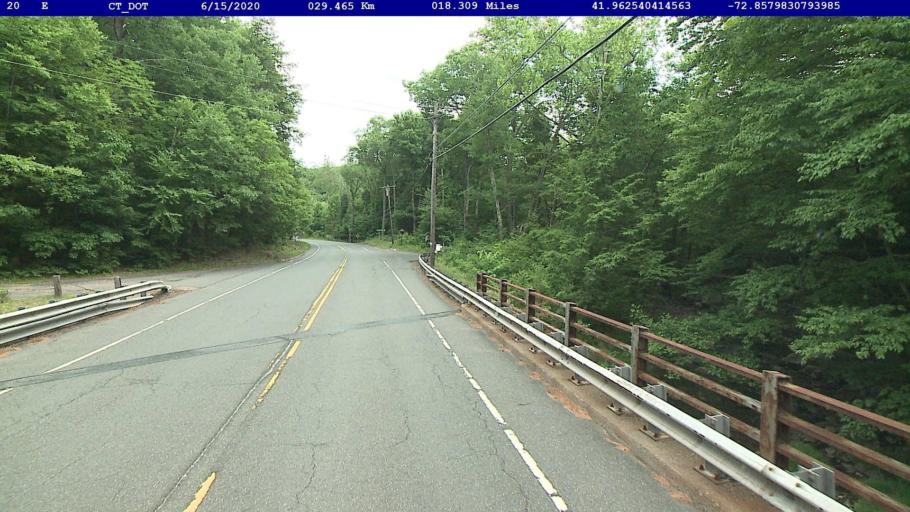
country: US
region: Connecticut
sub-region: Hartford County
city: North Granby
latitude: 41.9625
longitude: -72.8580
